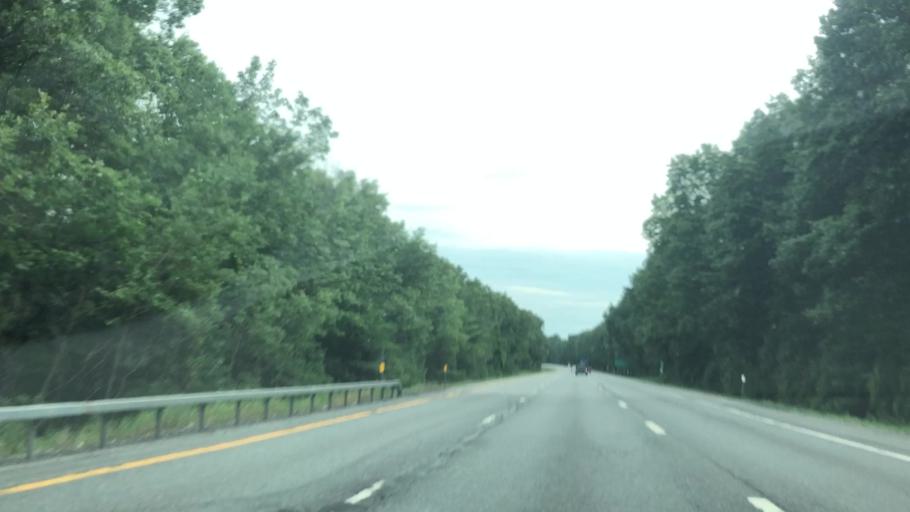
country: US
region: New York
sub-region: Saratoga County
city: Saratoga Springs
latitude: 43.1135
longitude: -73.7484
